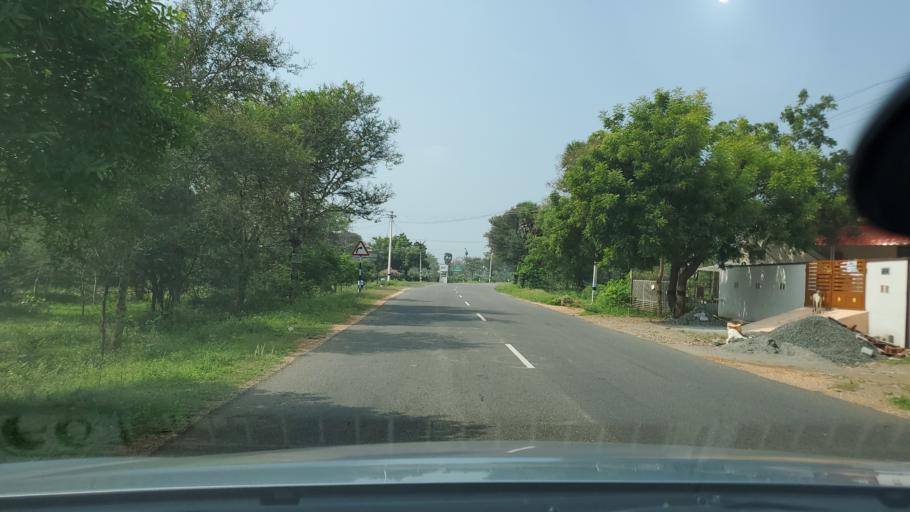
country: IN
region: Tamil Nadu
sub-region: Erode
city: Chennimalai
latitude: 11.1929
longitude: 77.6246
